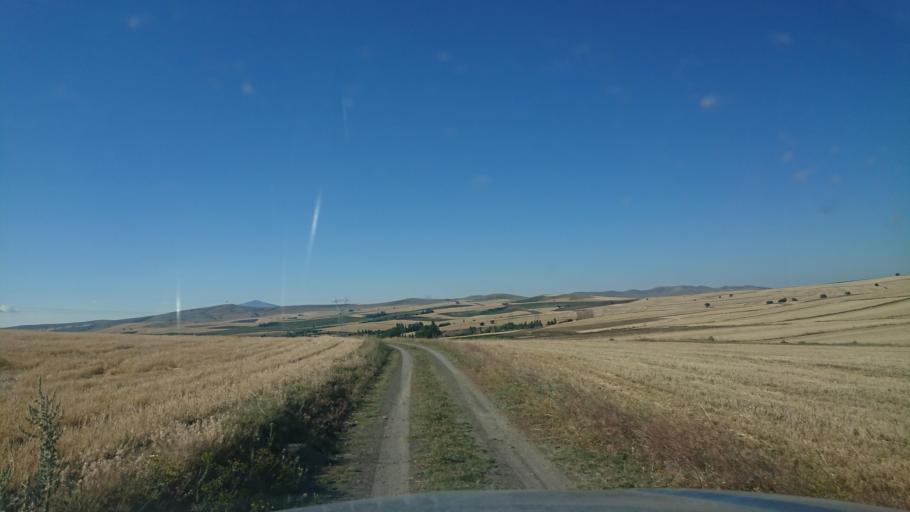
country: TR
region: Aksaray
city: Agacoren
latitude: 38.8310
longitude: 33.9427
